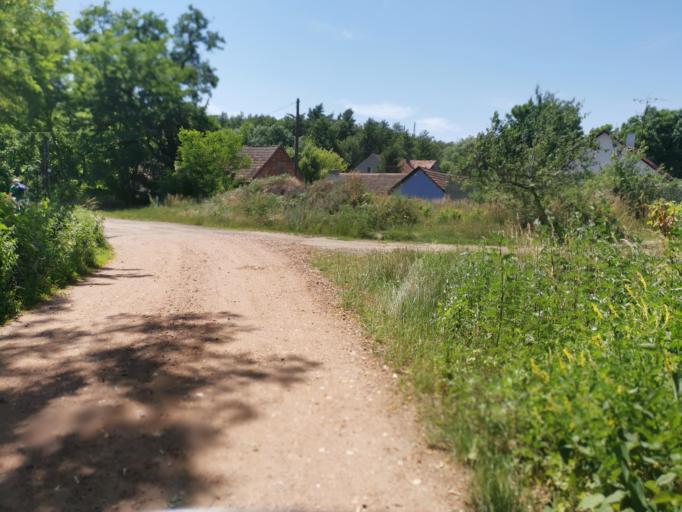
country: CZ
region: South Moravian
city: Rohatec
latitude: 48.9015
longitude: 17.2159
